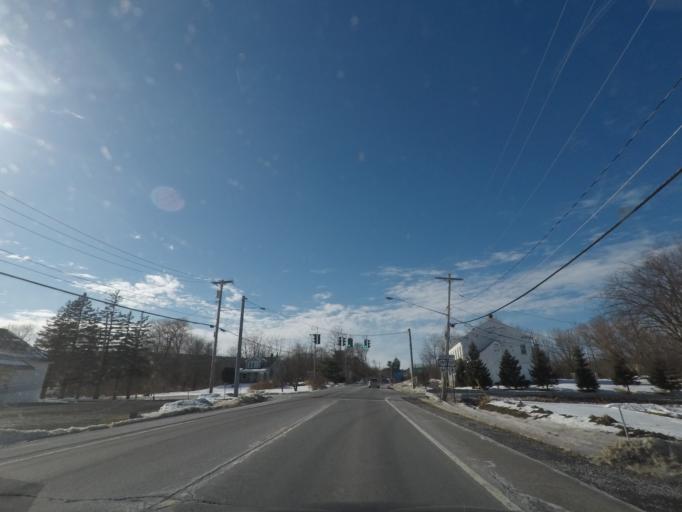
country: US
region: New York
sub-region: Albany County
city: Altamont
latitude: 42.7395
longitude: -74.0135
